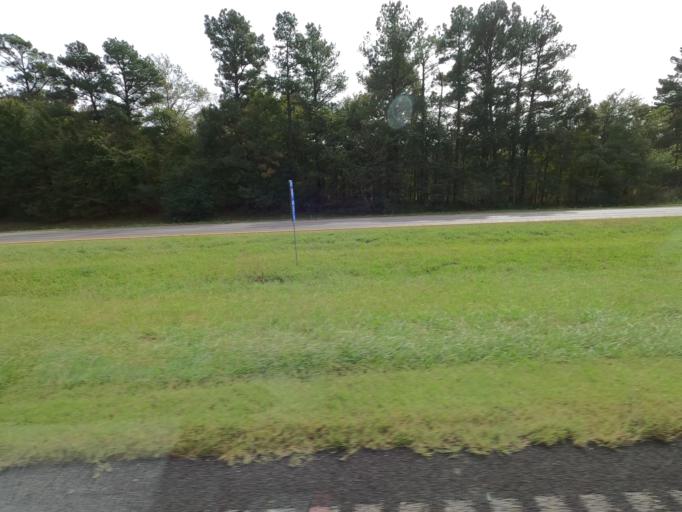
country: US
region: Tennessee
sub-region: Tipton County
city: Mason
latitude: 35.3727
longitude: -89.4665
